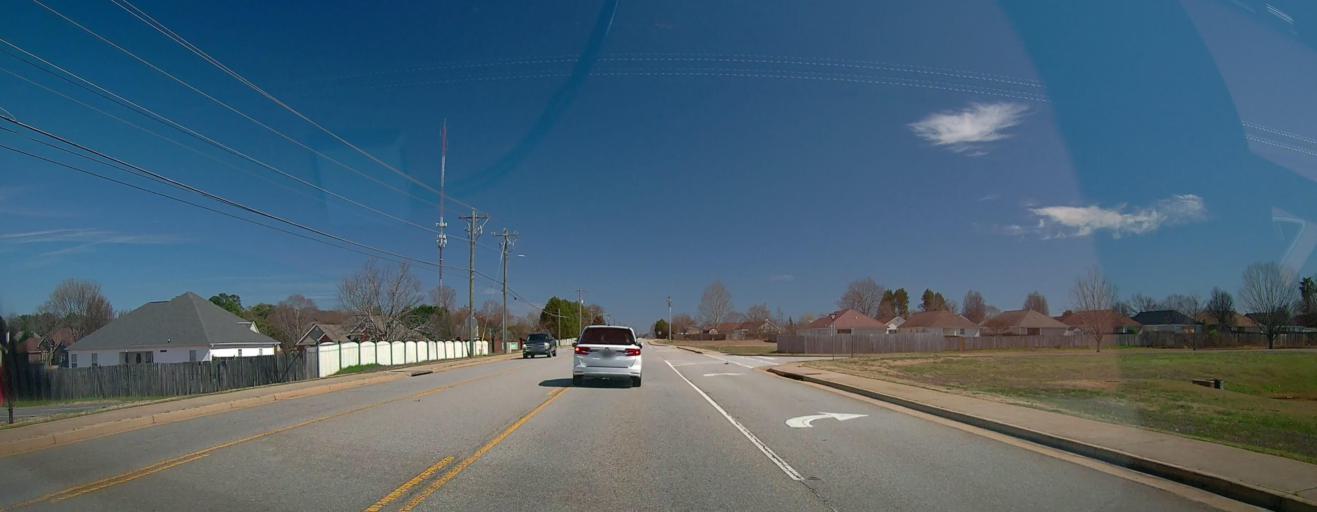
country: US
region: Georgia
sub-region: Houston County
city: Centerville
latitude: 32.5710
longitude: -83.6754
